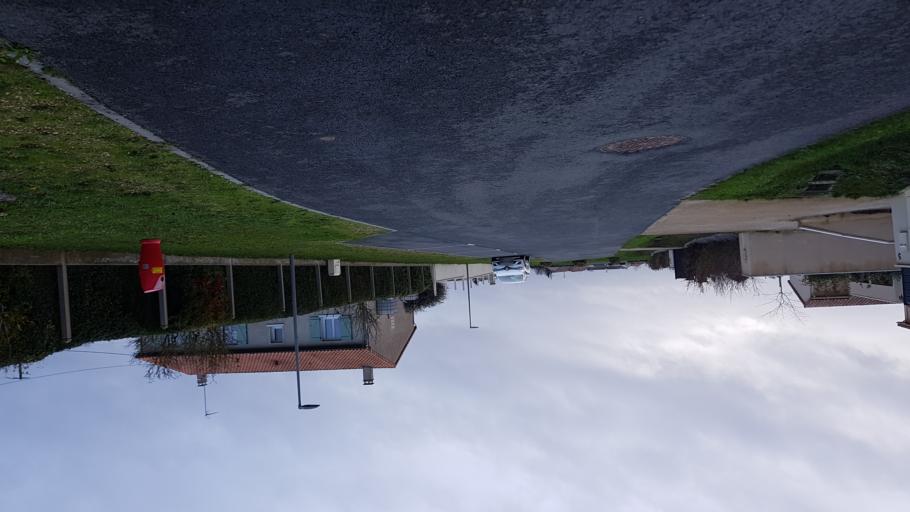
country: FR
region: Poitou-Charentes
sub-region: Departement de la Vienne
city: Avanton
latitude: 46.6616
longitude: 0.3096
